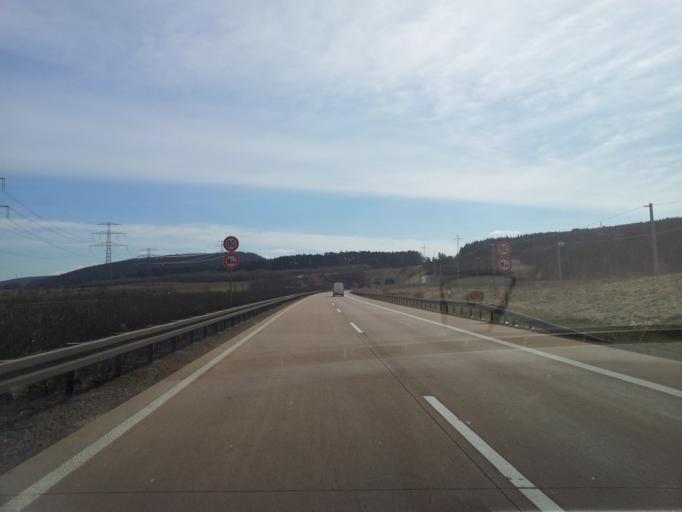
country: DE
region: Thuringia
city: Behringen
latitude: 50.7856
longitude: 11.0045
